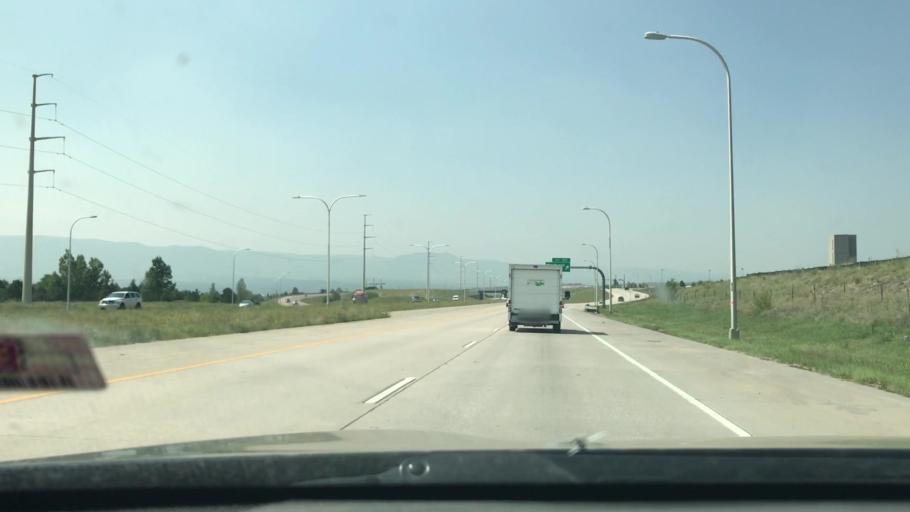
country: US
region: Colorado
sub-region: El Paso County
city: Black Forest
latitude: 38.9807
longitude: -104.7589
